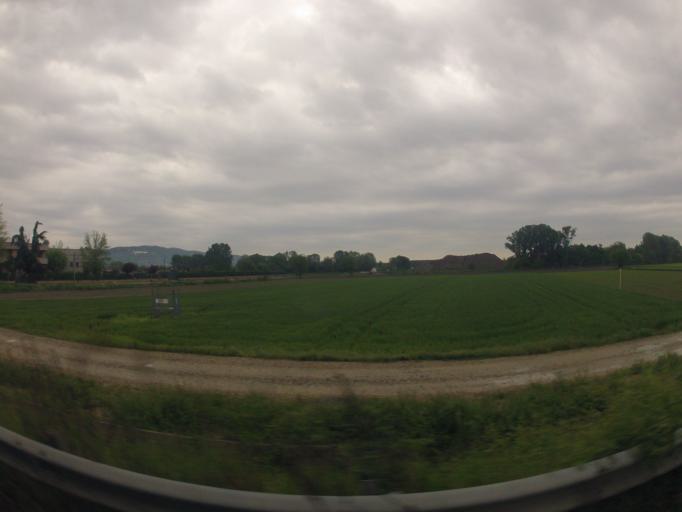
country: IT
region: Piedmont
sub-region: Provincia di Torino
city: La Loggia
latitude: 44.9641
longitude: 7.6767
